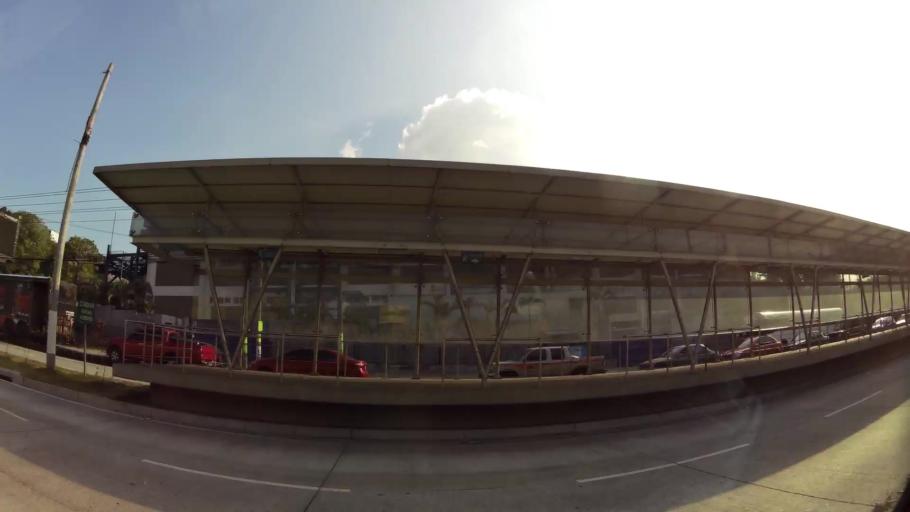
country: SV
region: San Salvador
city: Delgado
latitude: 13.7013
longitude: -89.1636
